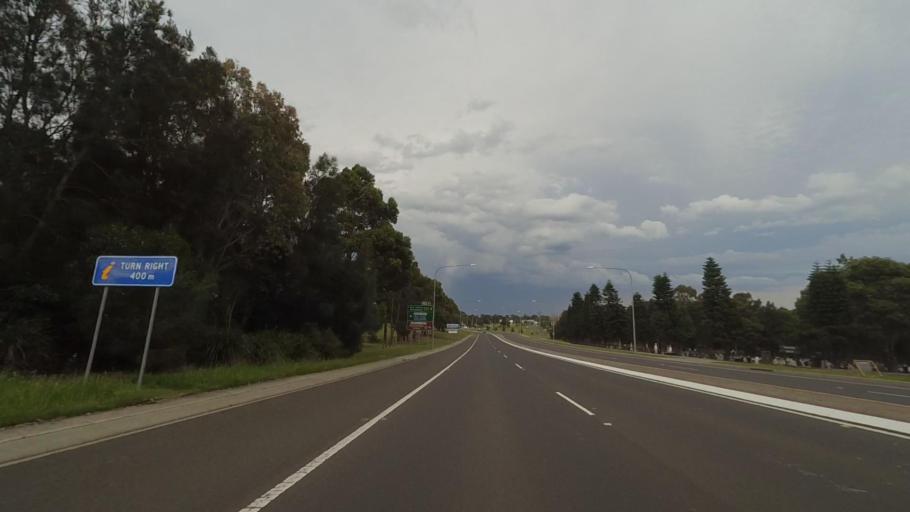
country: AU
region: New South Wales
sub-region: Shellharbour
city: Flinders
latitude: -34.5838
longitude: 150.8578
